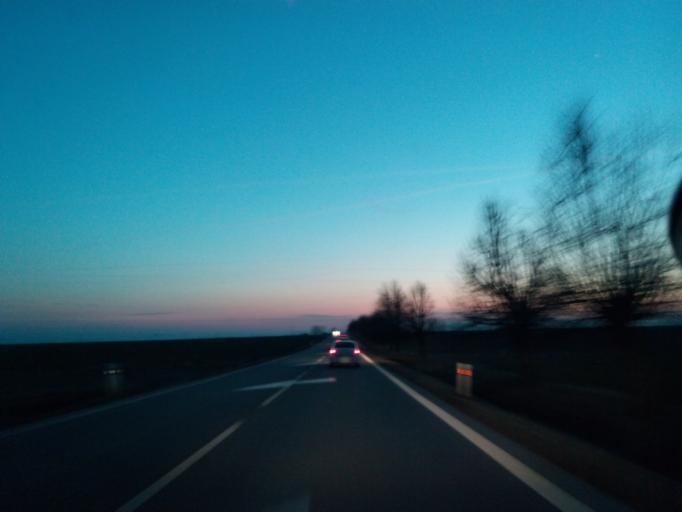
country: SK
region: Kosicky
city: Michalovce
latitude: 48.7029
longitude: 21.8179
